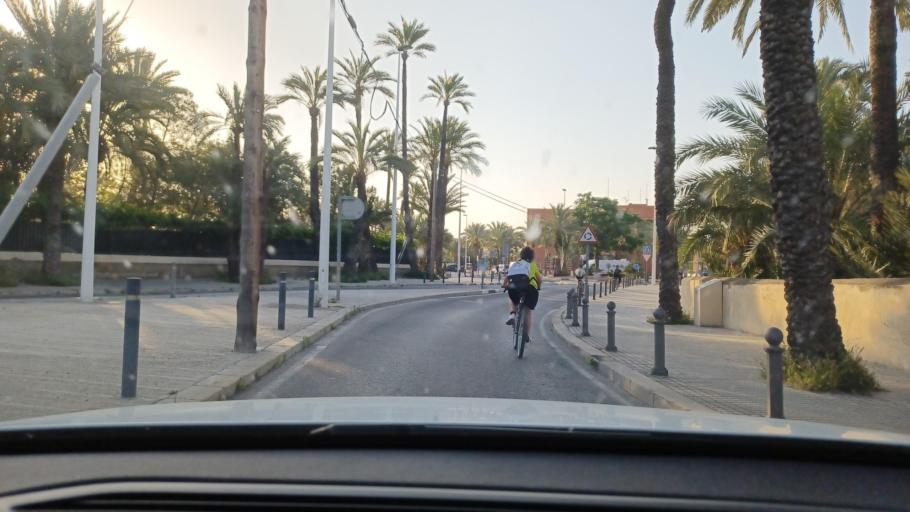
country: ES
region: Valencia
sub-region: Provincia de Alicante
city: Elche
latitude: 38.2634
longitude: -0.6893
